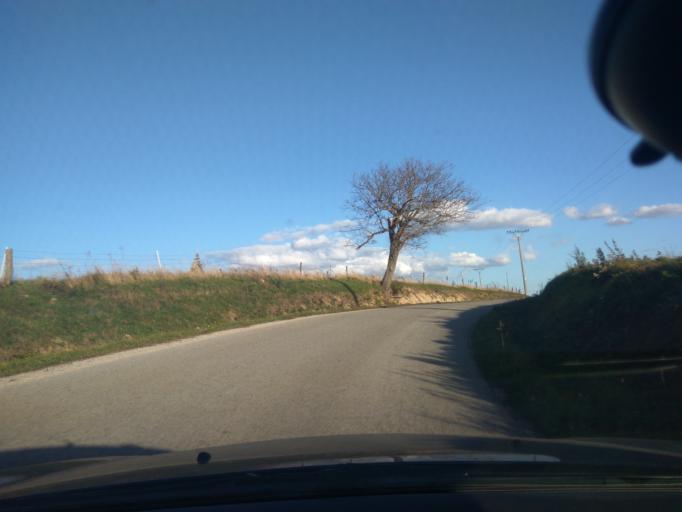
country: SK
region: Nitriansky
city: Brezova pod Bradlom
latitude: 48.6723
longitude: 17.6010
